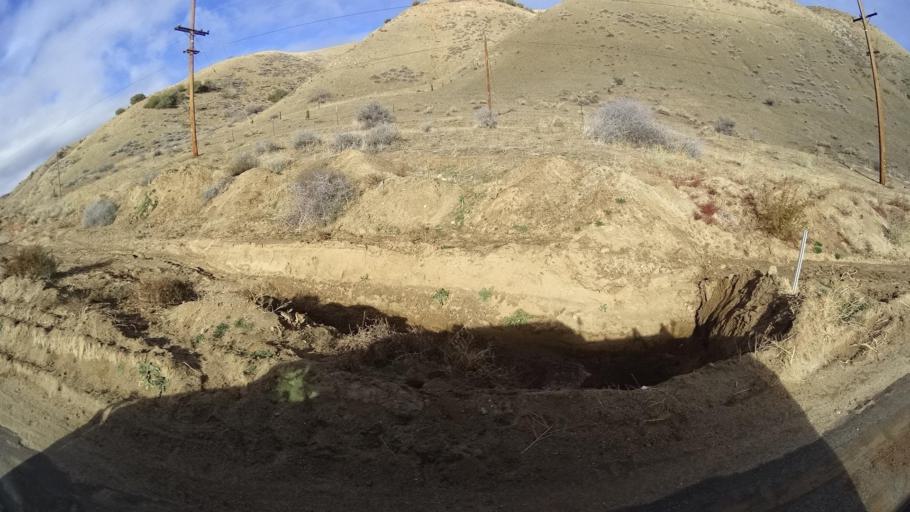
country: US
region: California
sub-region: Kern County
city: Mojave
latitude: 35.0911
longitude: -118.3094
